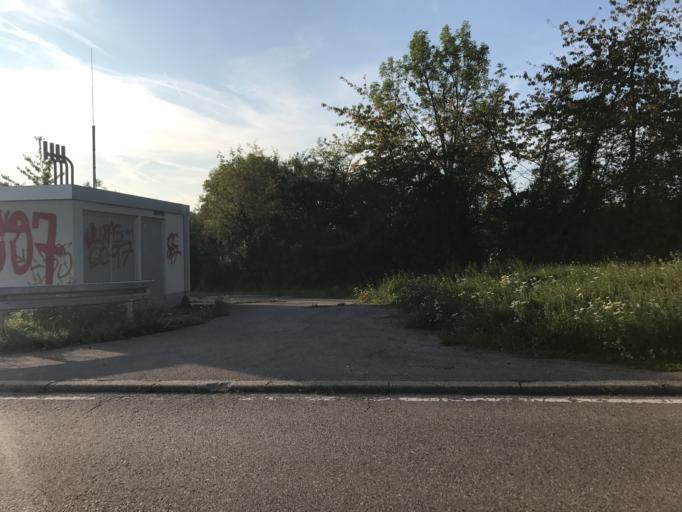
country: DE
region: Baden-Wuerttemberg
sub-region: Regierungsbezirk Stuttgart
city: Korntal
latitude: 48.8269
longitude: 9.1249
